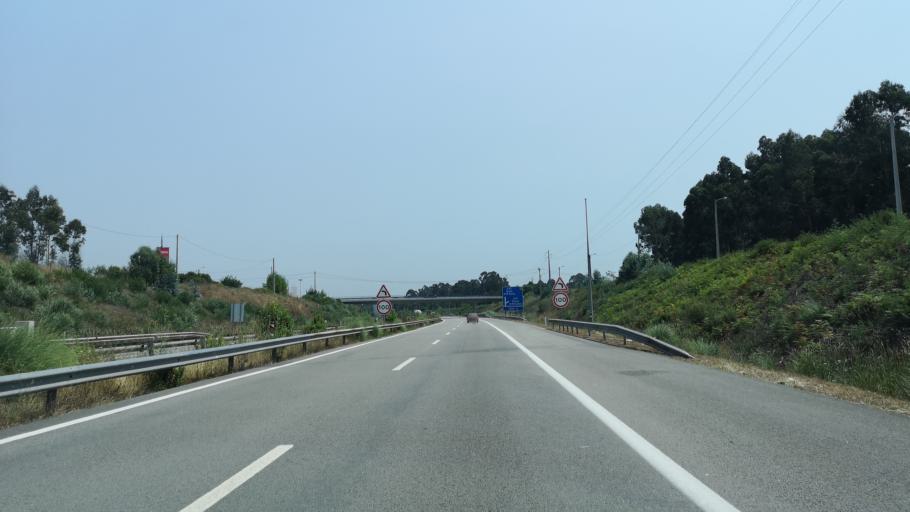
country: PT
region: Aveiro
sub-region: Aveiro
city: Aveiro
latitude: 40.6458
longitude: -8.6113
